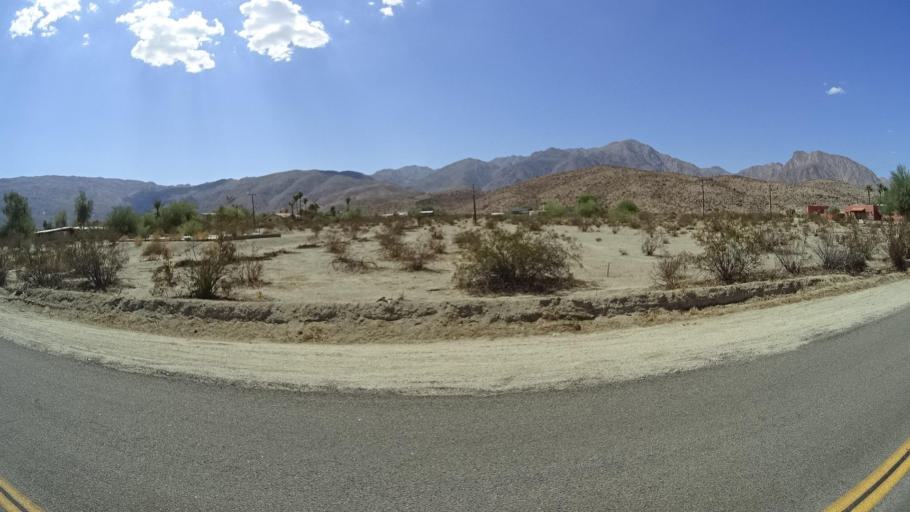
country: US
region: California
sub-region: San Diego County
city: Borrego Springs
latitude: 33.2435
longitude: -116.3761
